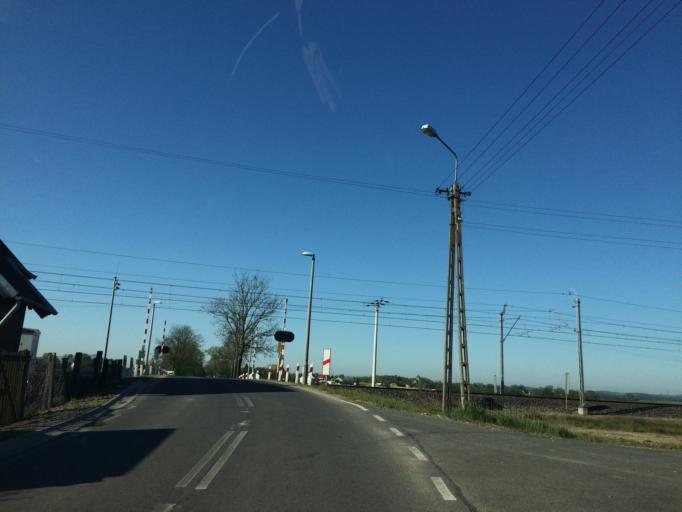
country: PL
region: Warmian-Masurian Voivodeship
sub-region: Powiat ilawski
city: Lubawa
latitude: 53.4213
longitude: 19.7732
